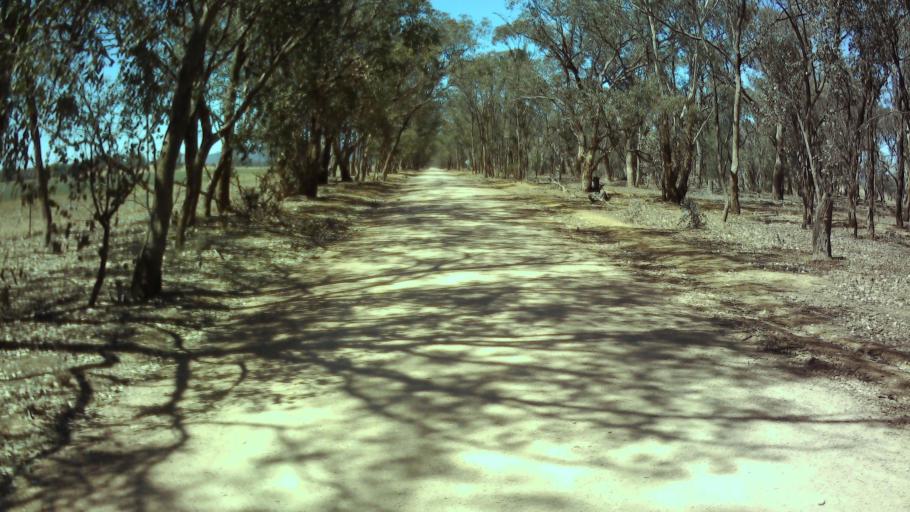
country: AU
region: New South Wales
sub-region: Weddin
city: Grenfell
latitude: -33.9079
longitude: 148.0803
